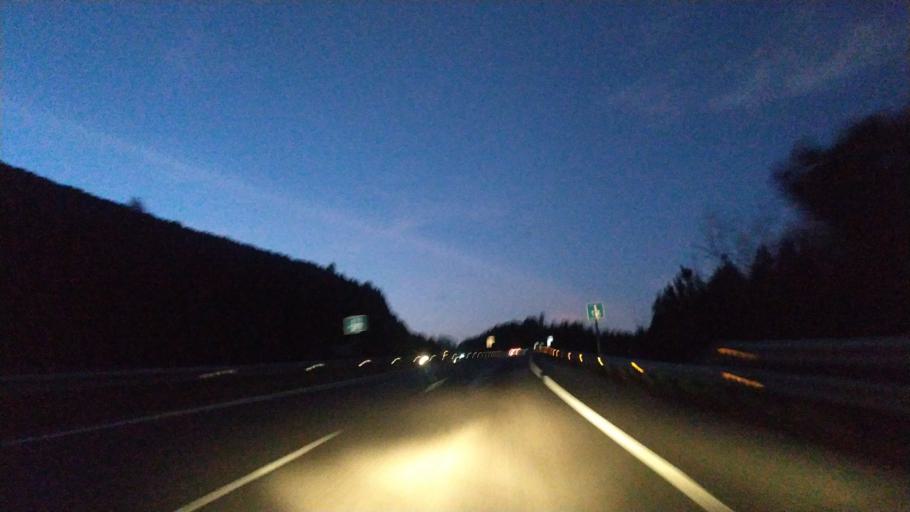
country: ES
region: Asturias
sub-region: Province of Asturias
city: Muros de Nalon
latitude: 43.5302
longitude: -6.0991
